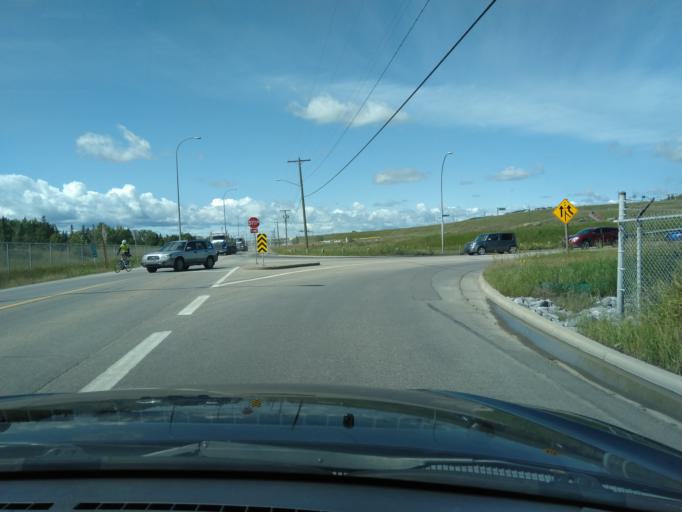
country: CA
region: Alberta
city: Calgary
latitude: 51.1021
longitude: -114.2155
